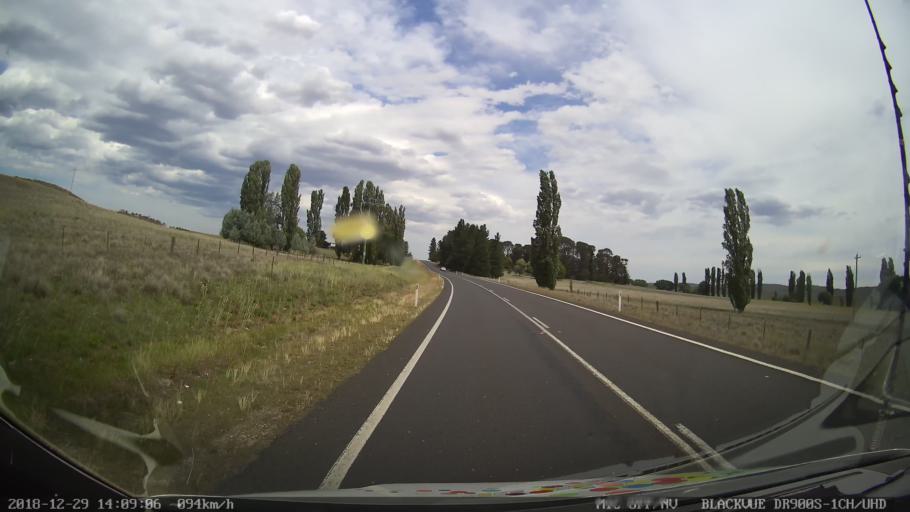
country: AU
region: New South Wales
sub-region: Cooma-Monaro
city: Cooma
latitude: -36.3743
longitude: 149.2123
